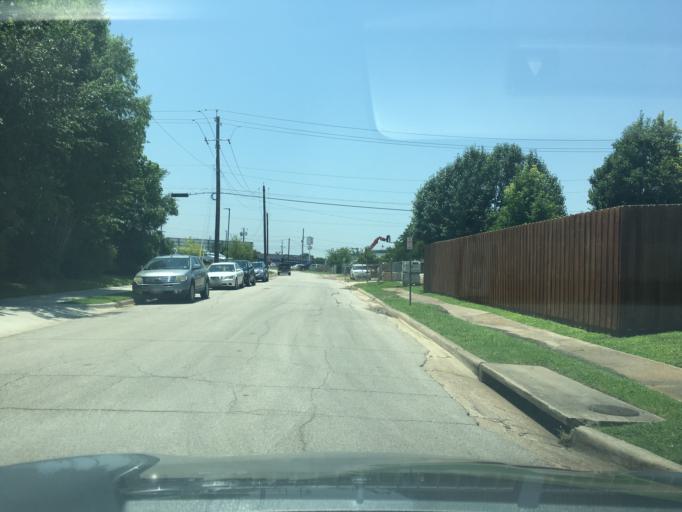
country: US
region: Texas
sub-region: Dallas County
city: Richardson
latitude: 32.9110
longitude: -96.6955
